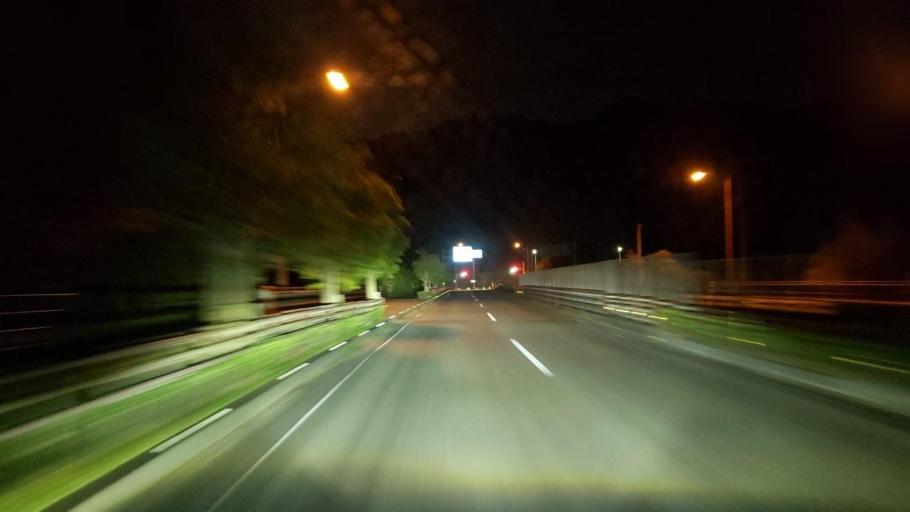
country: JP
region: Tokushima
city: Narutocho-mitsuishi
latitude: 34.1918
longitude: 134.5803
